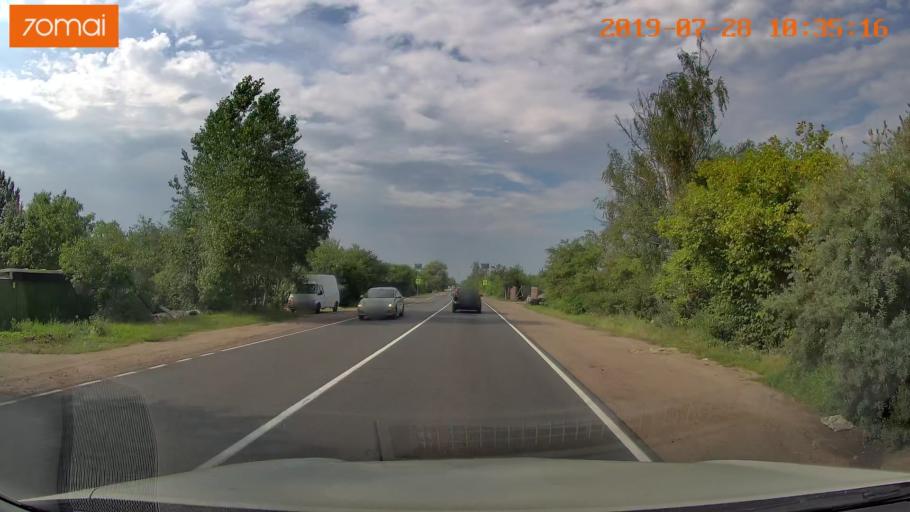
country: RU
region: Kaliningrad
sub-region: Gorod Kaliningrad
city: Kaliningrad
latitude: 54.7482
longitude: 20.4330
